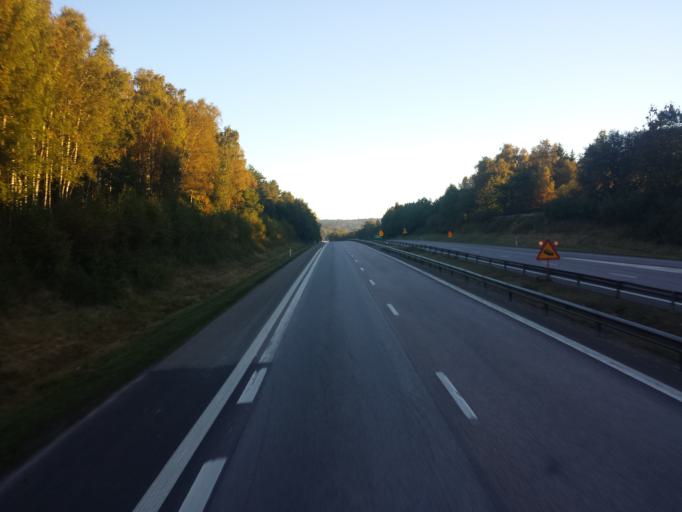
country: SE
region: Halland
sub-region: Kungsbacka Kommun
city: Kungsbacka
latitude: 57.4917
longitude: 12.0475
